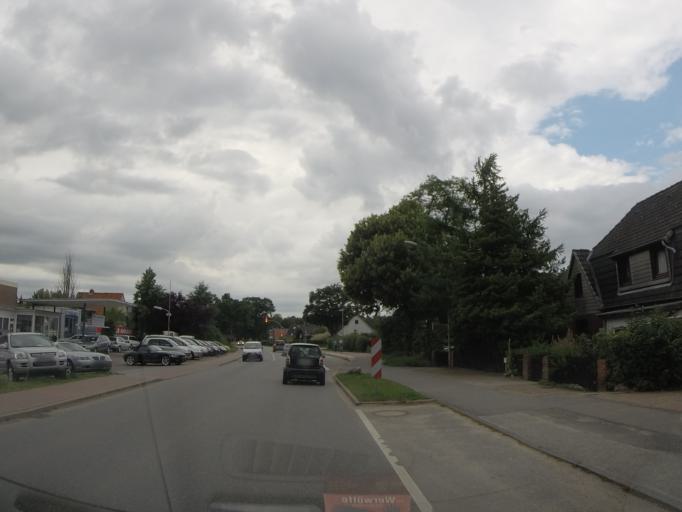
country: DE
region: Schleswig-Holstein
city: Ratekau
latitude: 53.9897
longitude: 10.7122
